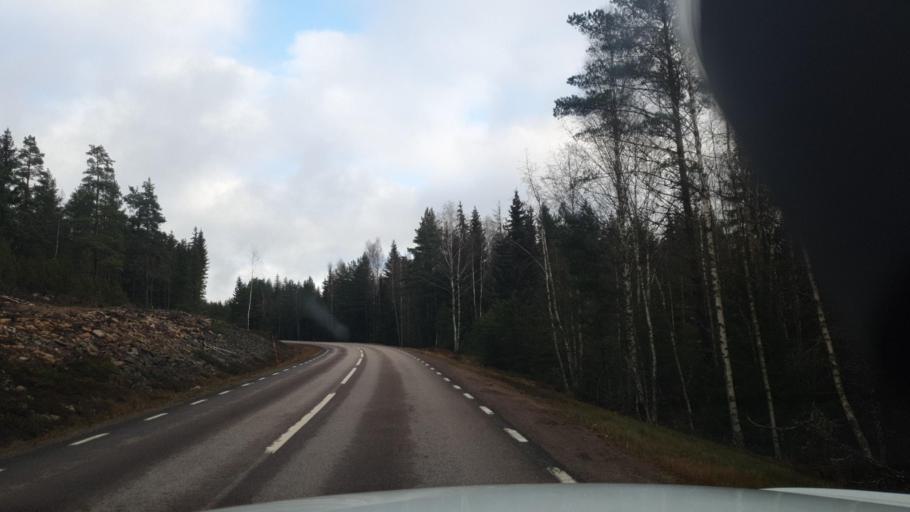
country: SE
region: Vaermland
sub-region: Sunne Kommun
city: Sunne
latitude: 59.6817
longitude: 13.0455
